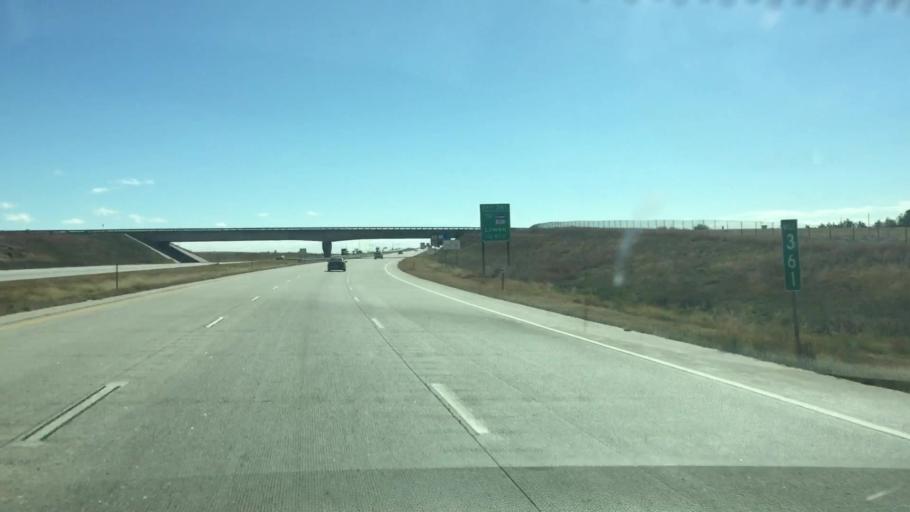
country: US
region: Colorado
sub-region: Lincoln County
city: Limon
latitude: 39.2715
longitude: -103.6796
